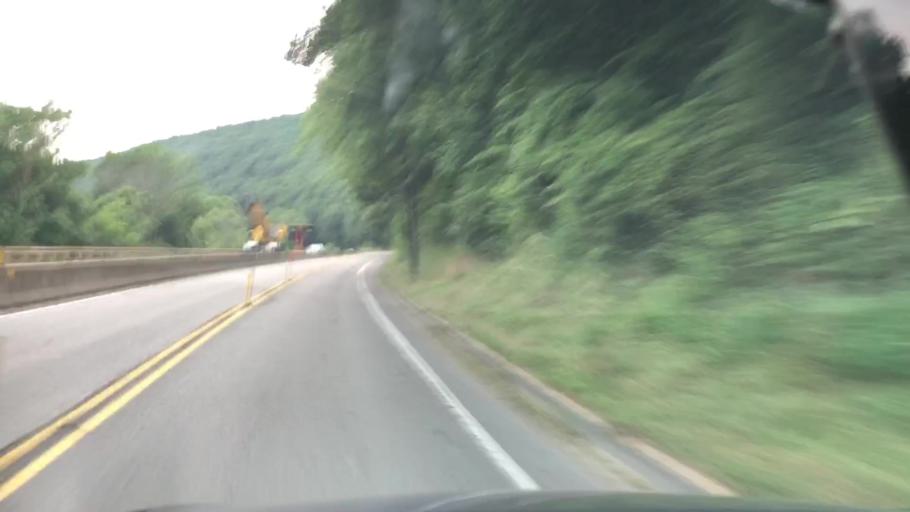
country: US
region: Pennsylvania
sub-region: Venango County
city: Oil City
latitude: 41.4288
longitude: -79.7236
